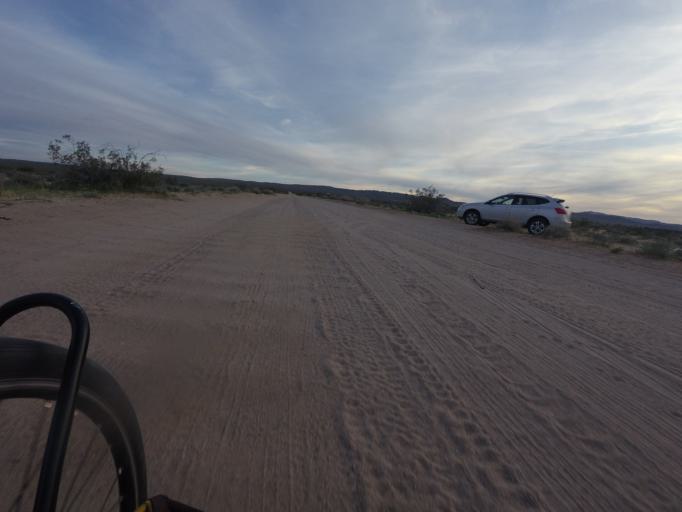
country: US
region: California
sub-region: Kern County
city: Ridgecrest
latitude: 35.6208
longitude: -117.6165
